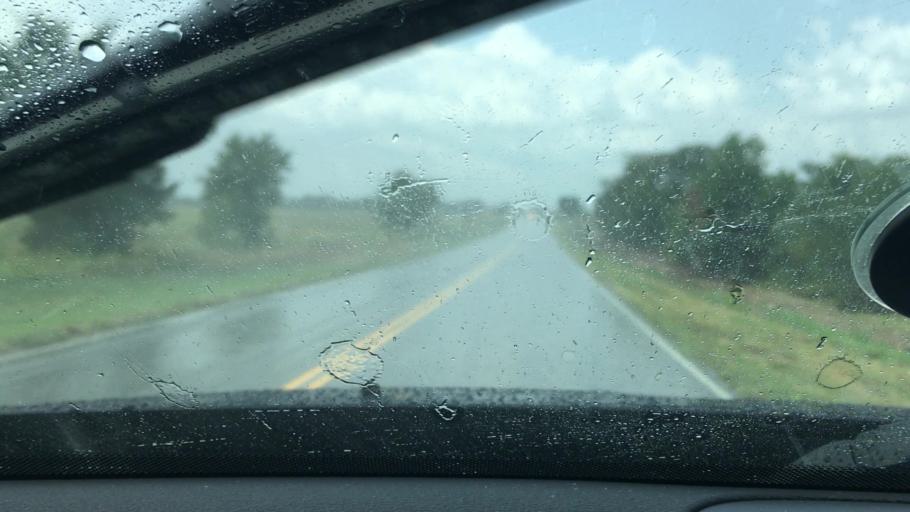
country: US
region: Oklahoma
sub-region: Johnston County
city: Tishomingo
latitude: 34.1749
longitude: -96.7137
